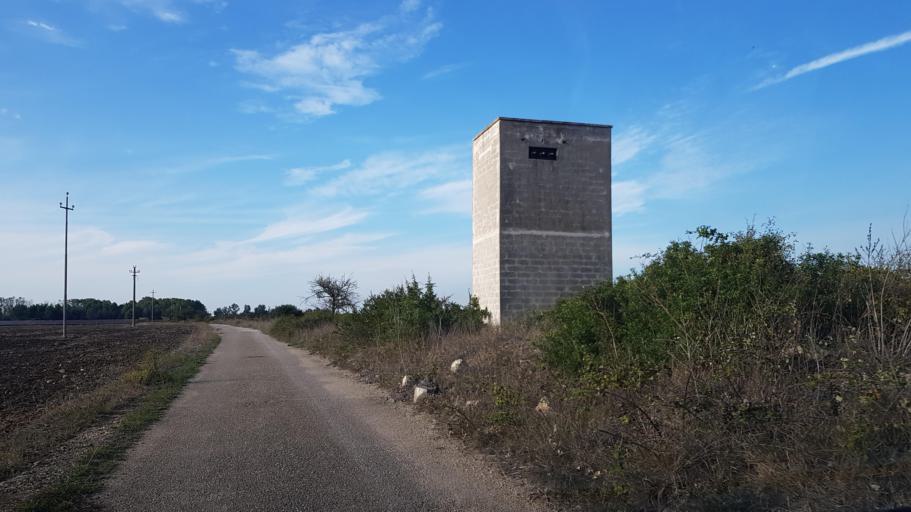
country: IT
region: Apulia
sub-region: Provincia di Brindisi
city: San Pancrazio Salentino
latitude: 40.4868
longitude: 17.8584
